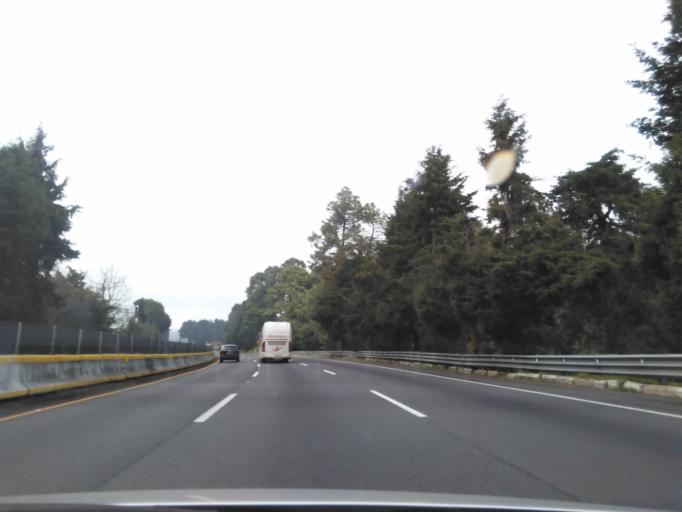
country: MX
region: Morelos
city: Tres Marias
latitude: 19.0469
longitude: -99.2368
